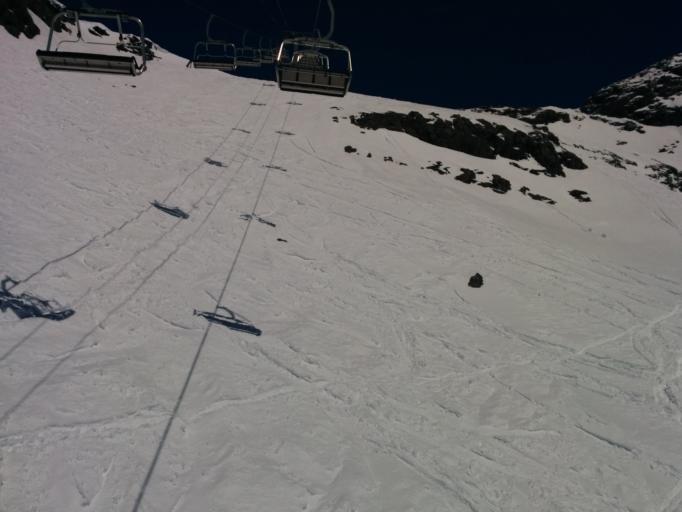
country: FR
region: Rhone-Alpes
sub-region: Departement de la Savoie
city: Val Thorens
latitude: 45.2546
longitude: 6.5974
